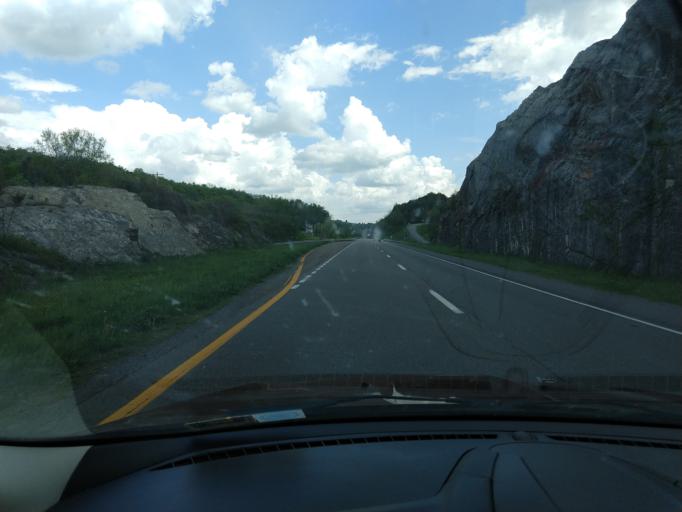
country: US
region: Virginia
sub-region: Tazewell County
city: Claypool Hill
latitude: 37.0435
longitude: -81.7870
